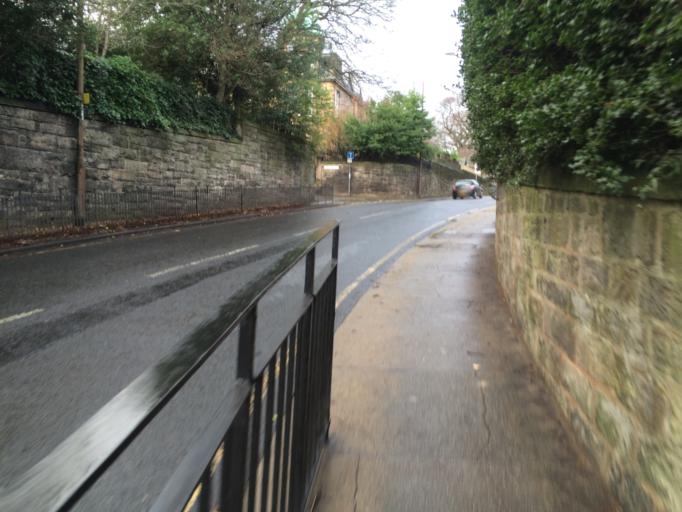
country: GB
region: Scotland
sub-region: Edinburgh
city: Edinburgh
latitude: 55.9505
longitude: -3.2243
